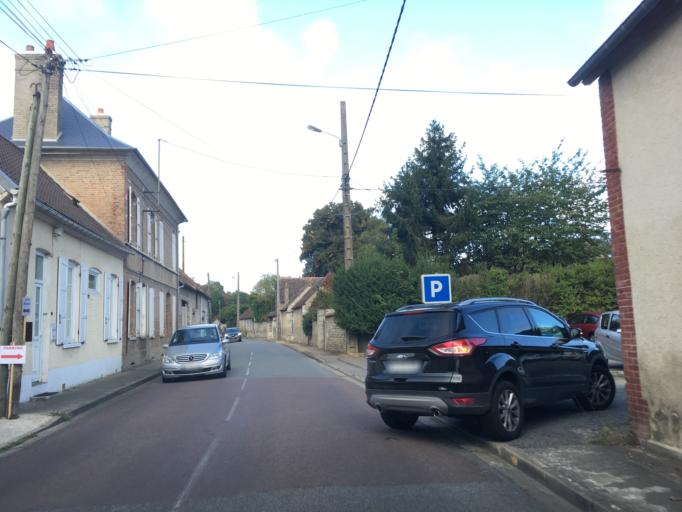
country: FR
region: Haute-Normandie
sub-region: Departement de l'Eure
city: Courcelles-sur-Seine
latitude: 49.1710
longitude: 1.4037
